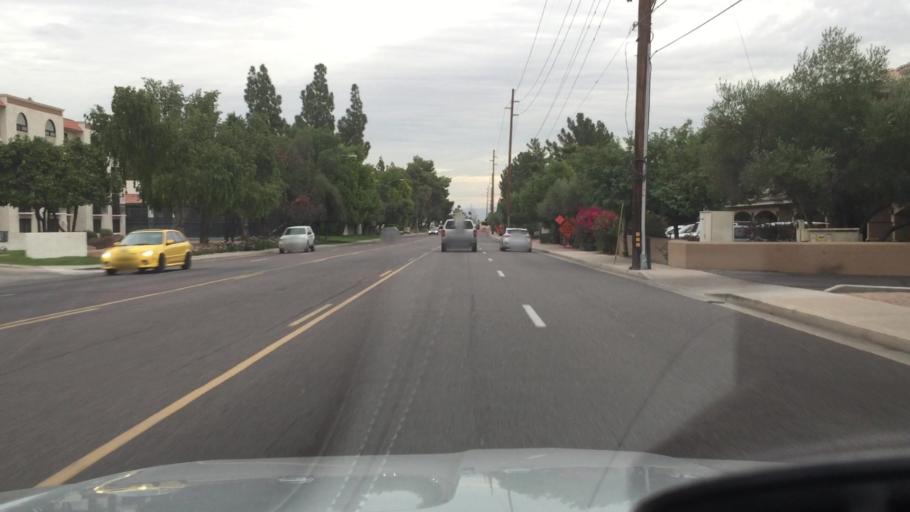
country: US
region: Arizona
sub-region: Maricopa County
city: Scottsdale
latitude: 33.5096
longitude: -111.9242
